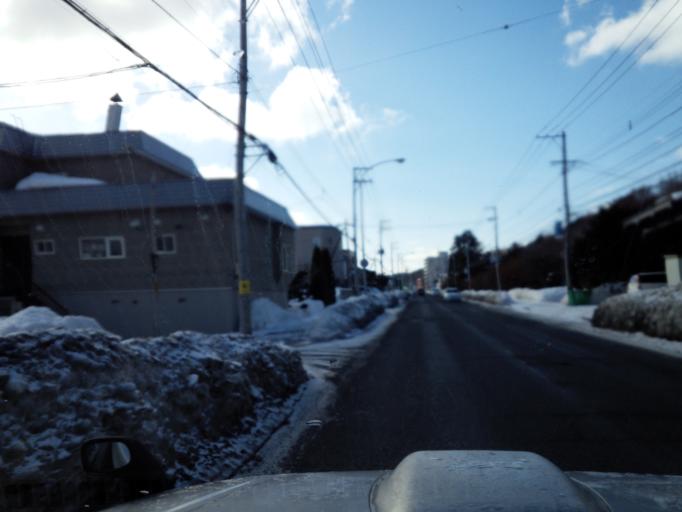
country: JP
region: Hokkaido
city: Sapporo
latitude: 42.9595
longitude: 141.3436
